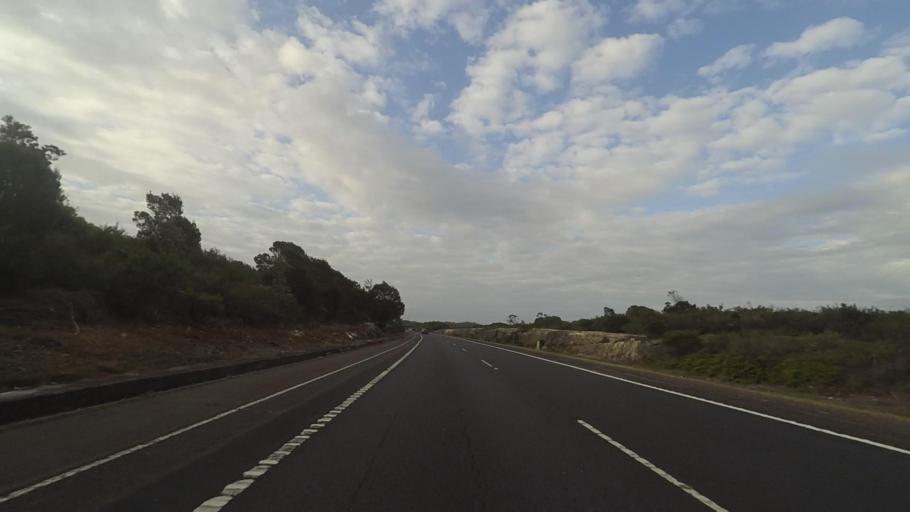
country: AU
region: New South Wales
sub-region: Wollongong
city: Bulli
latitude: -34.2800
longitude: 150.9282
